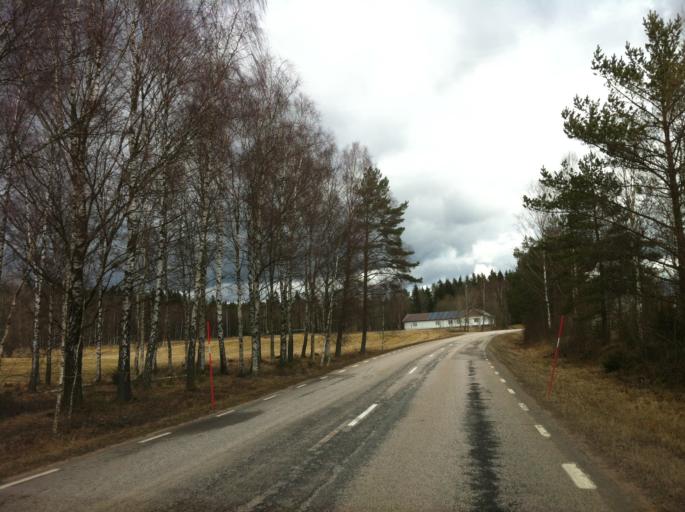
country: SE
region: Joenkoeping
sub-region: Gislaveds Kommun
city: Smalandsstenar
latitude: 57.2514
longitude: 13.2506
